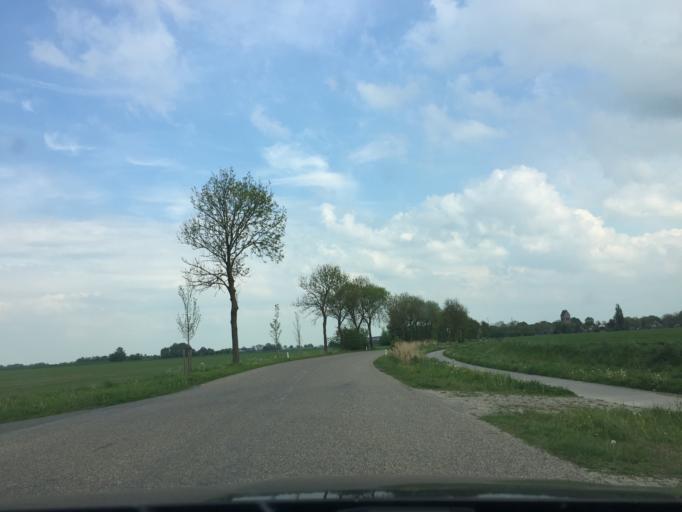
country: NL
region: Groningen
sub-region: Gemeente Zuidhorn
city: Oldehove
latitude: 53.3072
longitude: 6.3823
